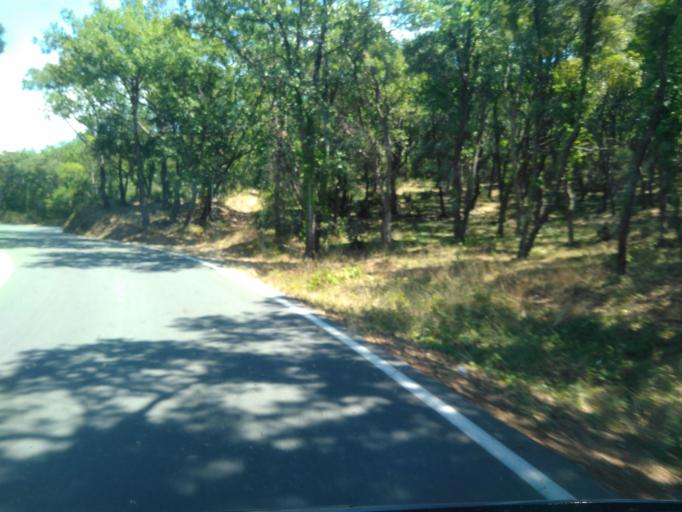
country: FR
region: Provence-Alpes-Cote d'Azur
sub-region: Departement du Var
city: La Croix-Valmer
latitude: 43.2108
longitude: 6.5733
